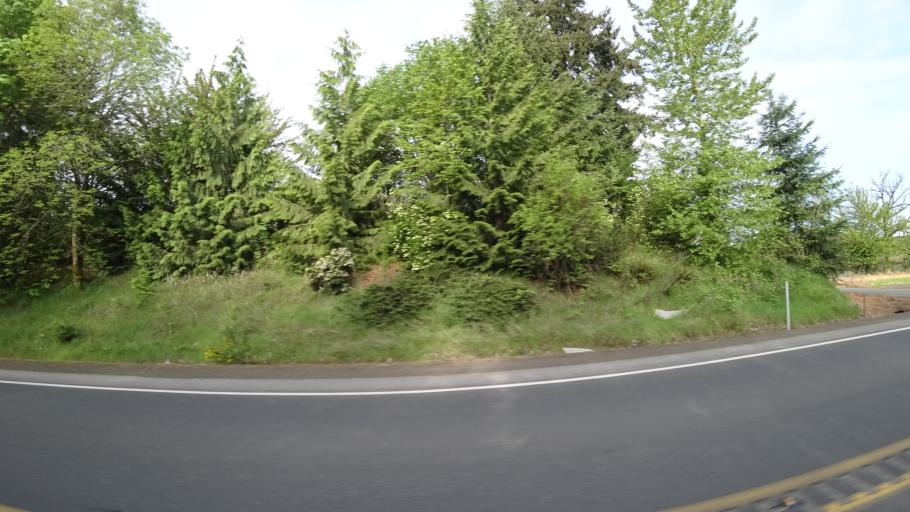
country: US
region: Oregon
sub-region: Washington County
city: Hillsboro
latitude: 45.4964
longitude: -122.9921
